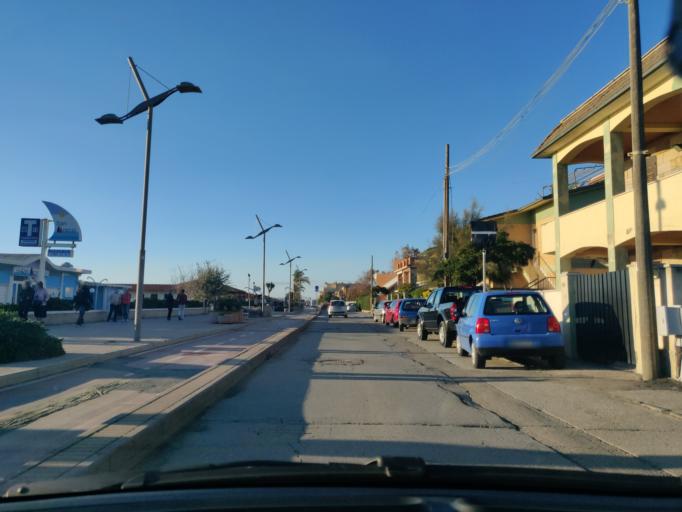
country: IT
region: Latium
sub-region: Provincia di Viterbo
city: Tarquinia
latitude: 42.2187
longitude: 11.7077
